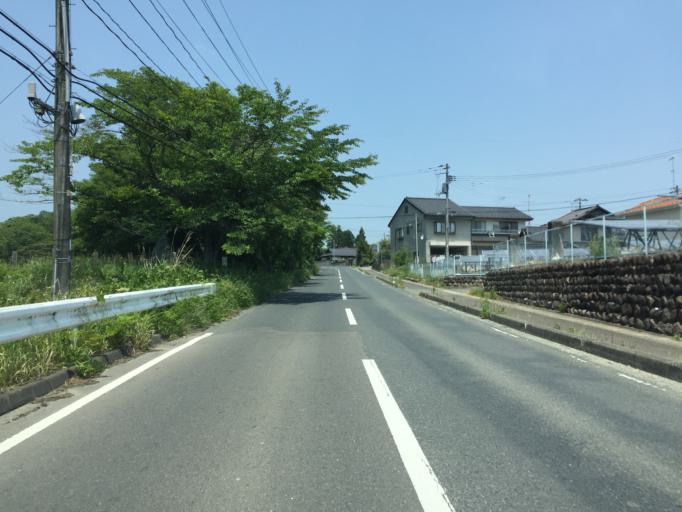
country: JP
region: Miyagi
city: Marumori
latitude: 37.8187
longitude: 140.8965
